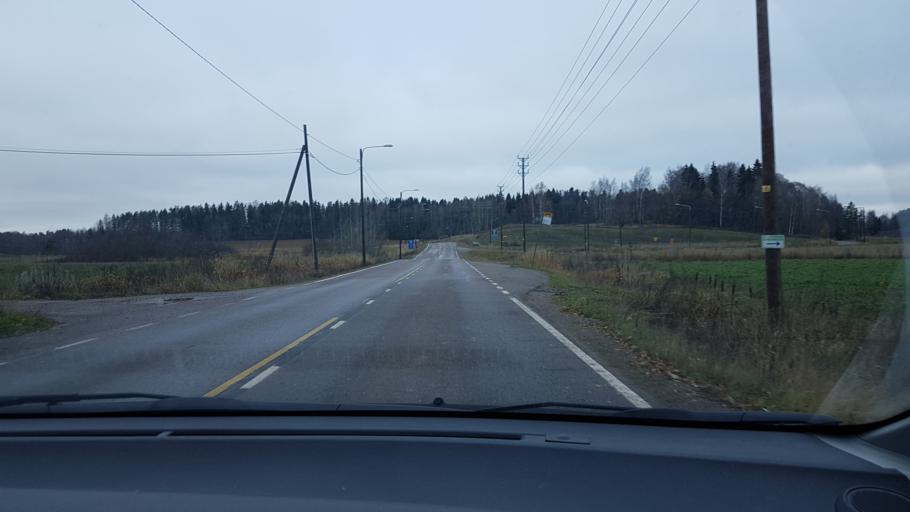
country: FI
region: Uusimaa
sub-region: Helsinki
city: Vantaa
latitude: 60.2753
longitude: 25.1379
